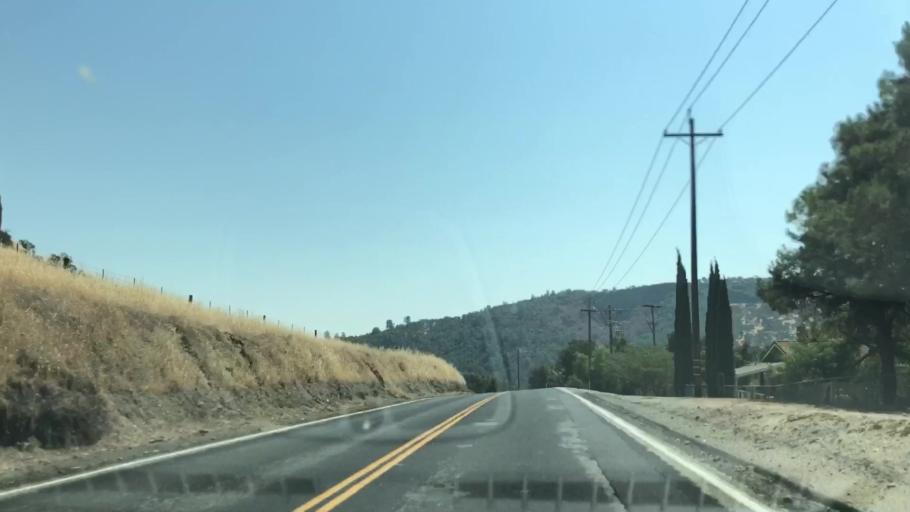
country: US
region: California
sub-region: Calaveras County
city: Copperopolis
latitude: 37.9017
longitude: -120.5807
